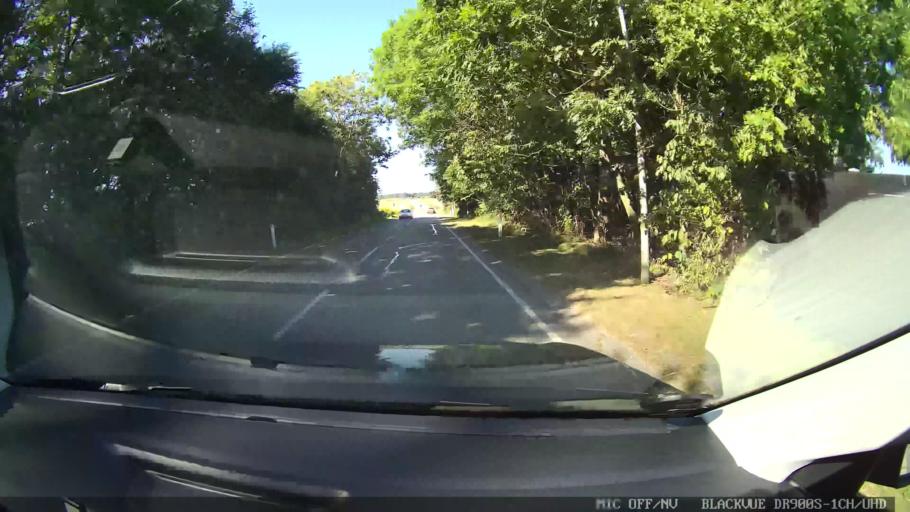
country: DK
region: Central Jutland
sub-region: Randers Kommune
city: Spentrup
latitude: 56.5270
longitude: 10.0018
